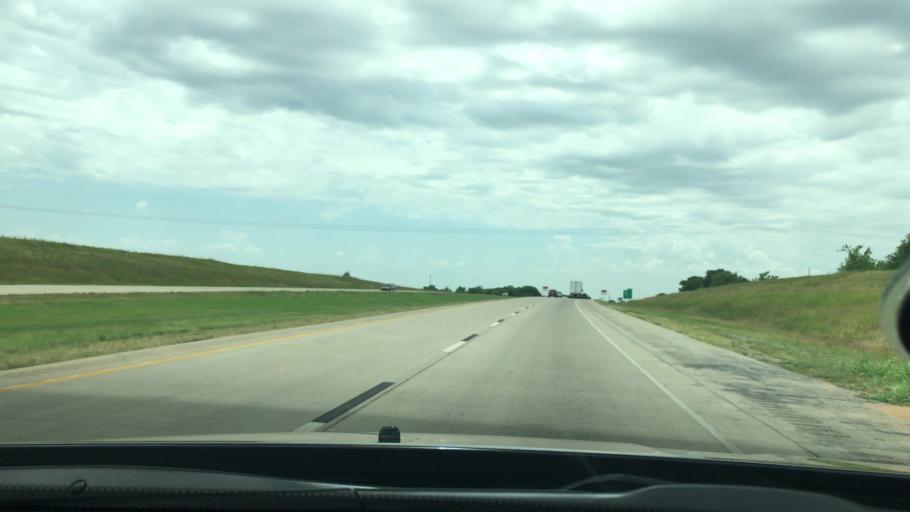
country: US
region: Oklahoma
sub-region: Love County
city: Marietta
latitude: 33.9623
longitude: -97.1343
